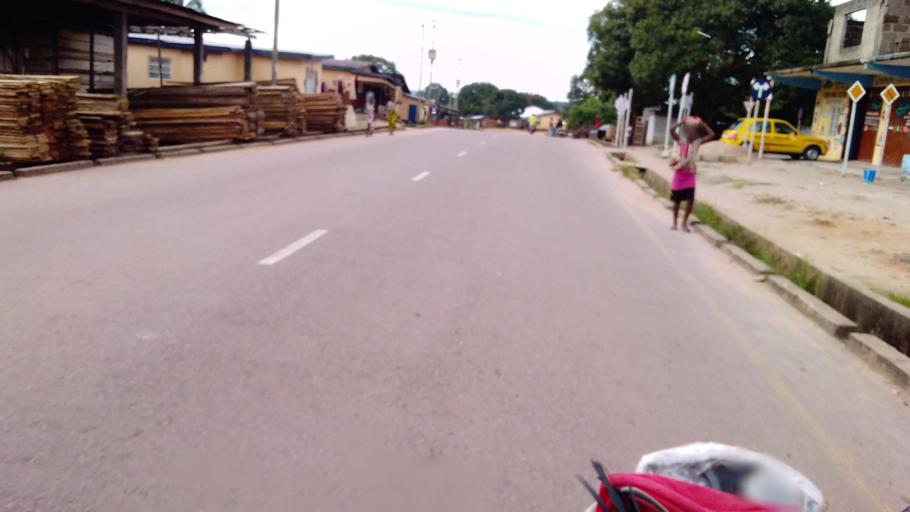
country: SL
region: Eastern Province
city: Koidu
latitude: 8.6513
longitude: -10.9754
